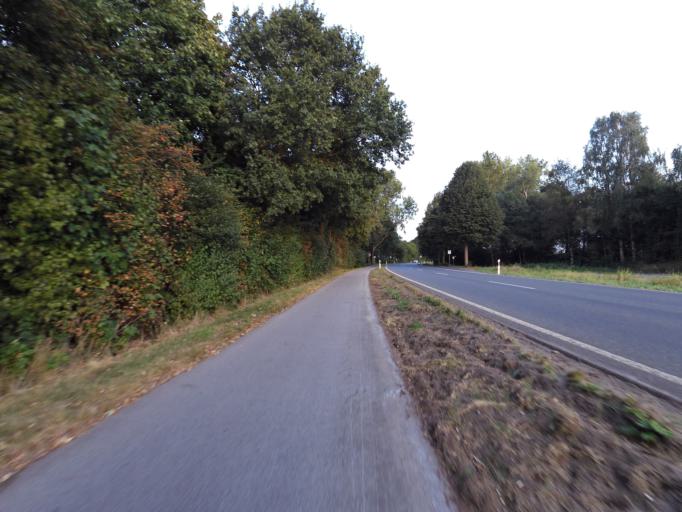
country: DE
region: North Rhine-Westphalia
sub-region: Regierungsbezirk Dusseldorf
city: Emmerich
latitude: 51.8612
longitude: 6.1839
